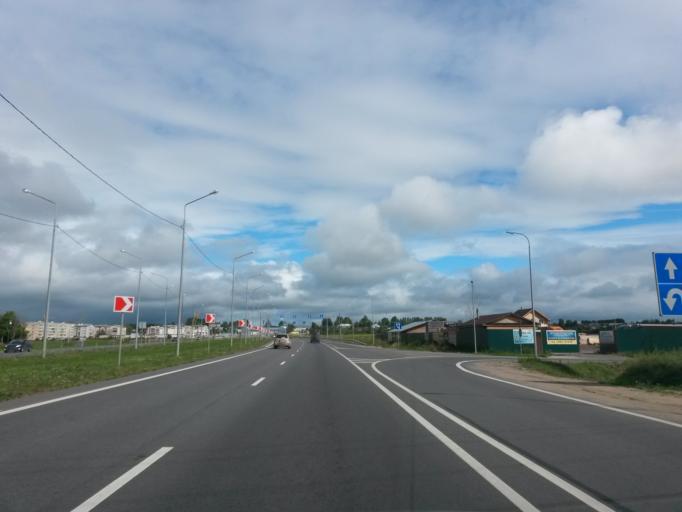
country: RU
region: Jaroslavl
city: Yaroslavl
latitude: 57.6959
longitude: 39.8991
